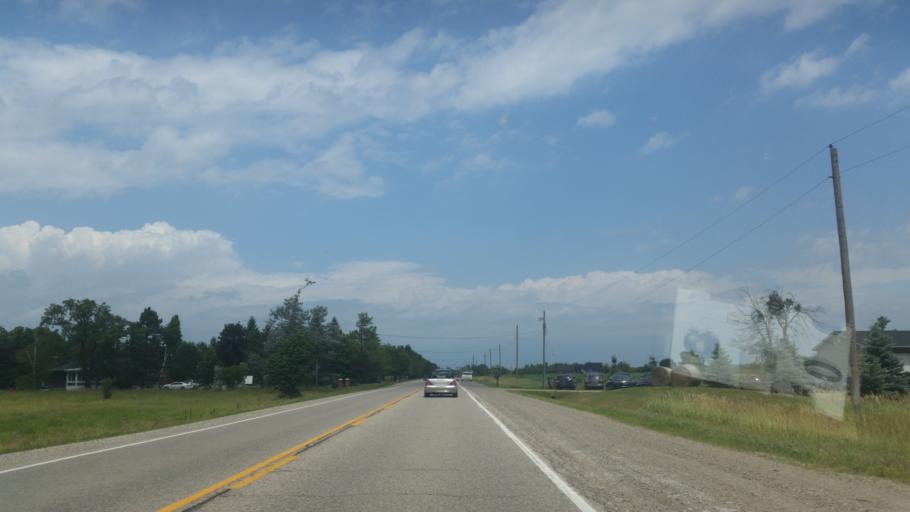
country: CA
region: Ontario
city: Orangeville
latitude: 43.7394
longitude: -80.0835
